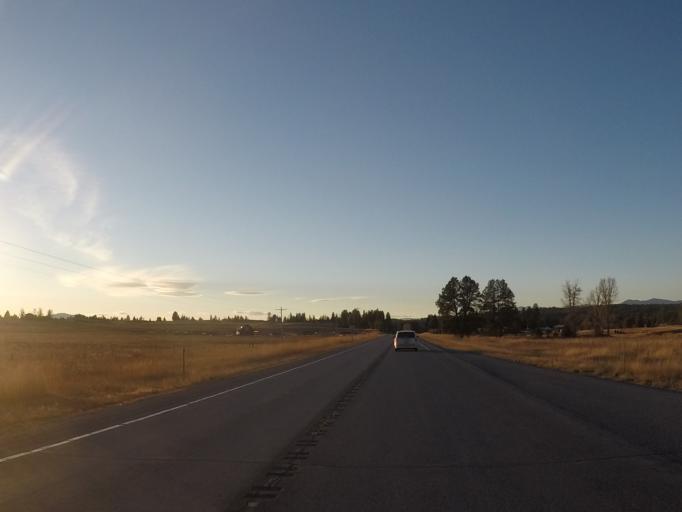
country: US
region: Montana
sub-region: Lewis and Clark County
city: Lincoln
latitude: 46.9950
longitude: -113.0245
